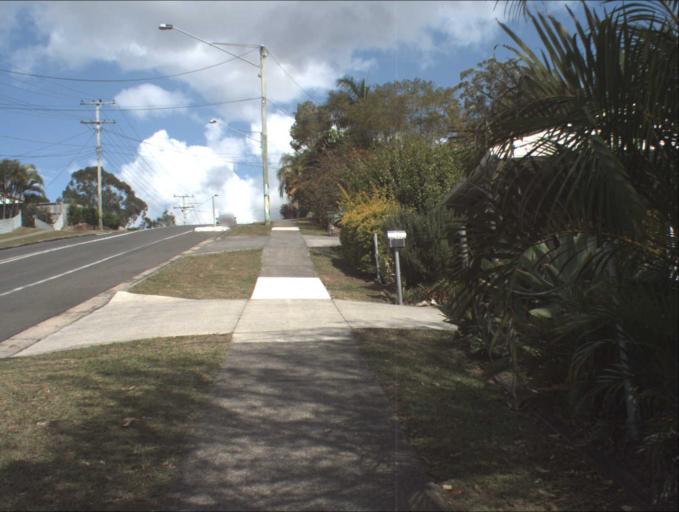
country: AU
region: Queensland
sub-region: Logan
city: Logan City
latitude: -27.6505
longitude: 153.1226
